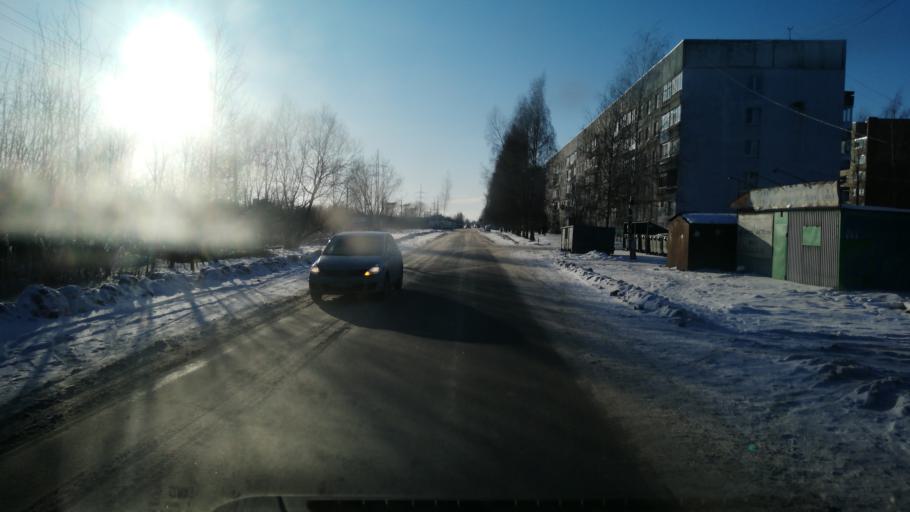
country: RU
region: Jaroslavl
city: Yaroslavl
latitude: 57.6172
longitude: 39.8010
